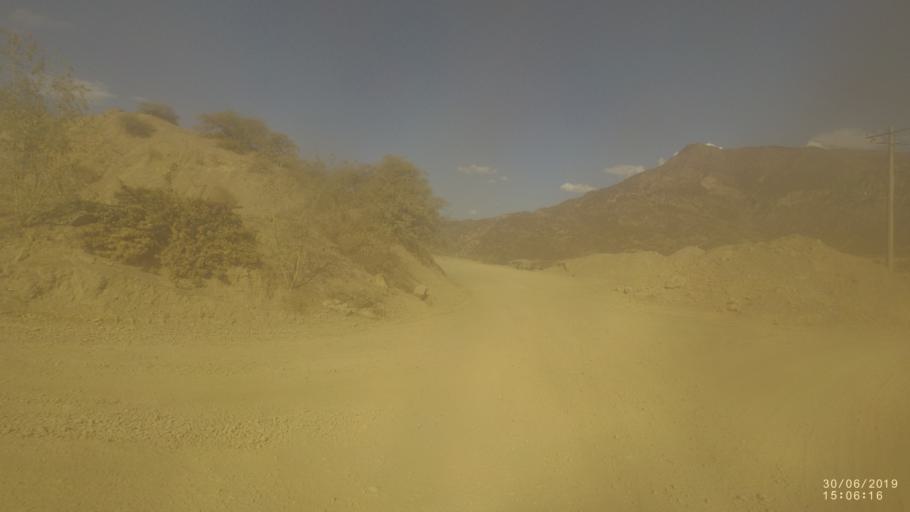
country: BO
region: Cochabamba
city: Irpa Irpa
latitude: -17.7318
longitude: -66.3120
